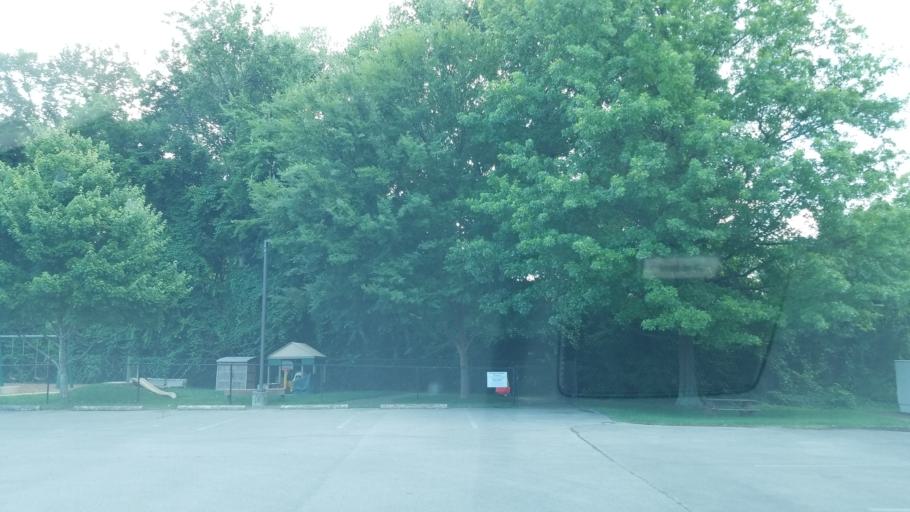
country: US
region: Tennessee
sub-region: Williamson County
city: Brentwood
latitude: 36.0290
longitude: -86.7944
